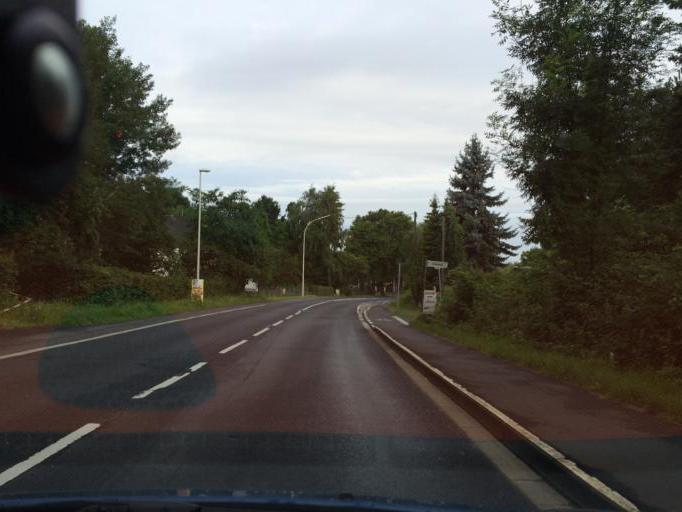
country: DE
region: North Rhine-Westphalia
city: Sankt Augustin
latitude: 50.7386
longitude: 7.1574
